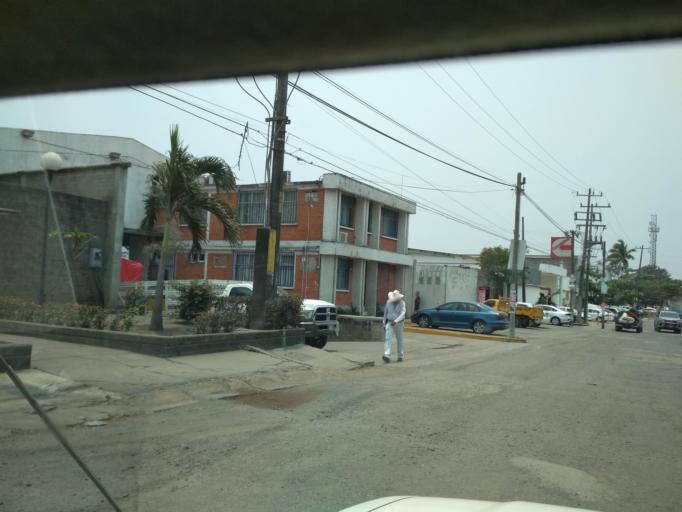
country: MX
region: Veracruz
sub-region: Veracruz
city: Lomas de Rio Medio Cuatro
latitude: 19.1704
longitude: -96.2311
